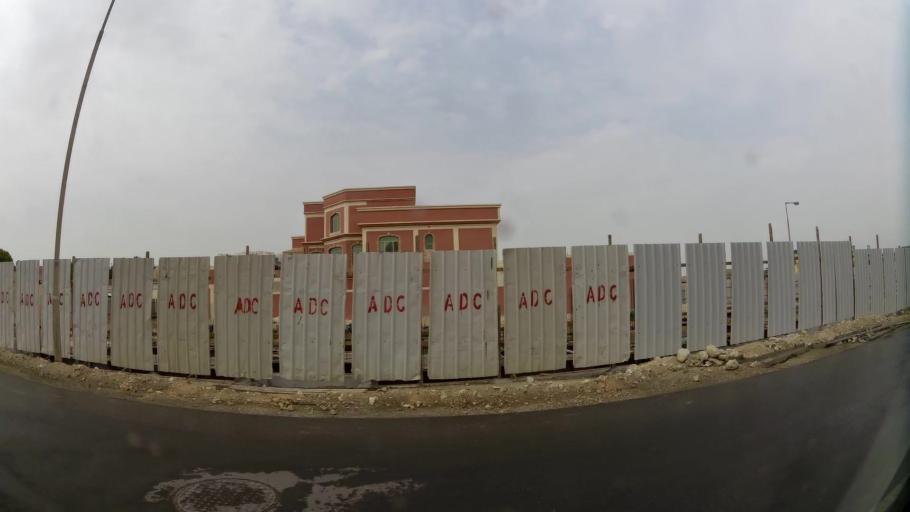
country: BH
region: Northern
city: Ar Rifa'
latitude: 26.1326
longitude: 50.5470
